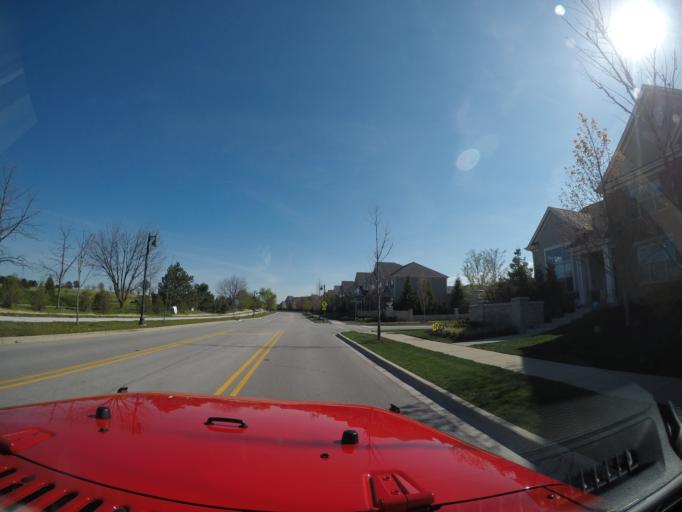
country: US
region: Illinois
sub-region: Cook County
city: Northbrook
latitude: 42.0923
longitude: -87.8318
